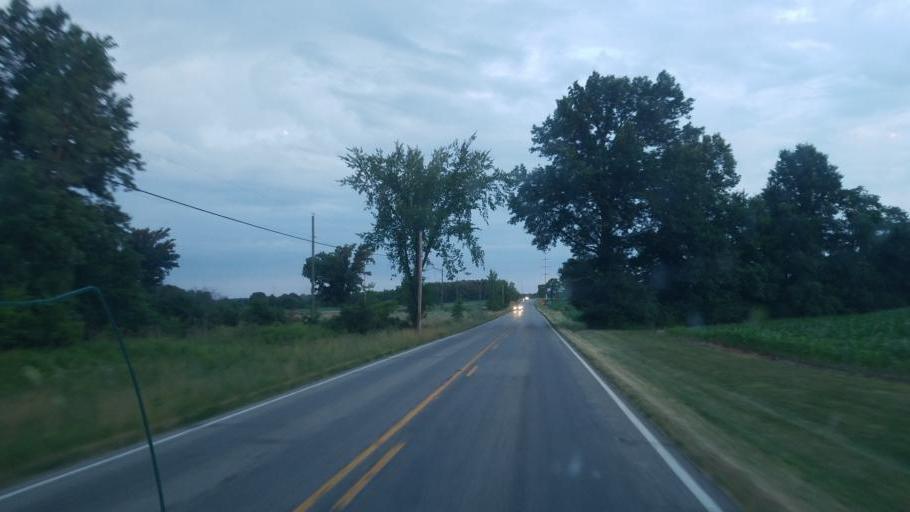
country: US
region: Ohio
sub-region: Defiance County
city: Hicksville
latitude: 41.3363
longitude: -84.8199
